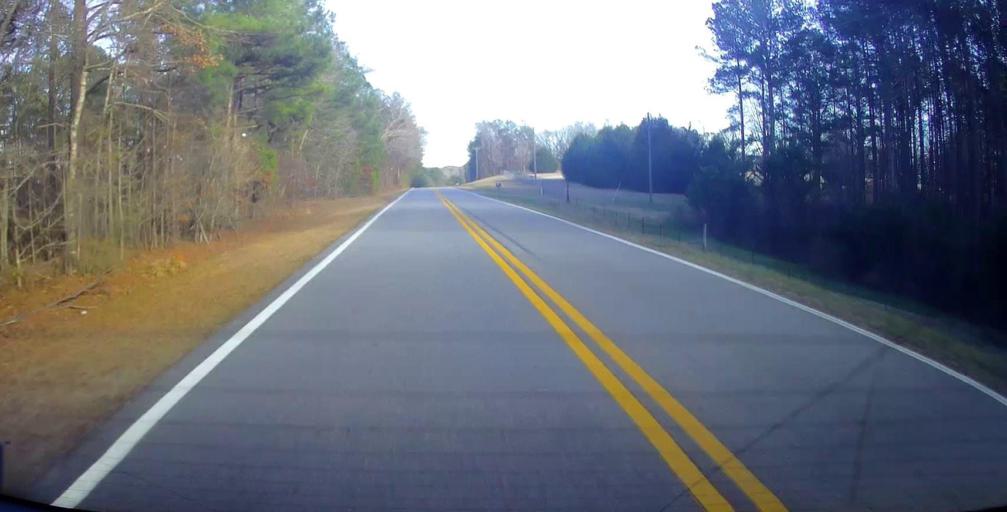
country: US
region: Georgia
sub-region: Bibb County
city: West Point
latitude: 32.8389
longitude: -83.9079
